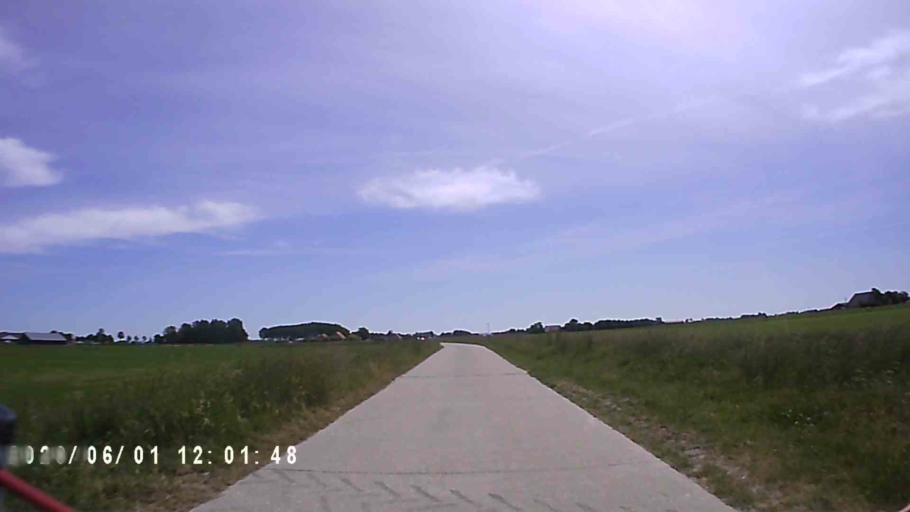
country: NL
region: Friesland
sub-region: Gemeente Harlingen
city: Harlingen
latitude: 53.1588
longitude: 5.4555
